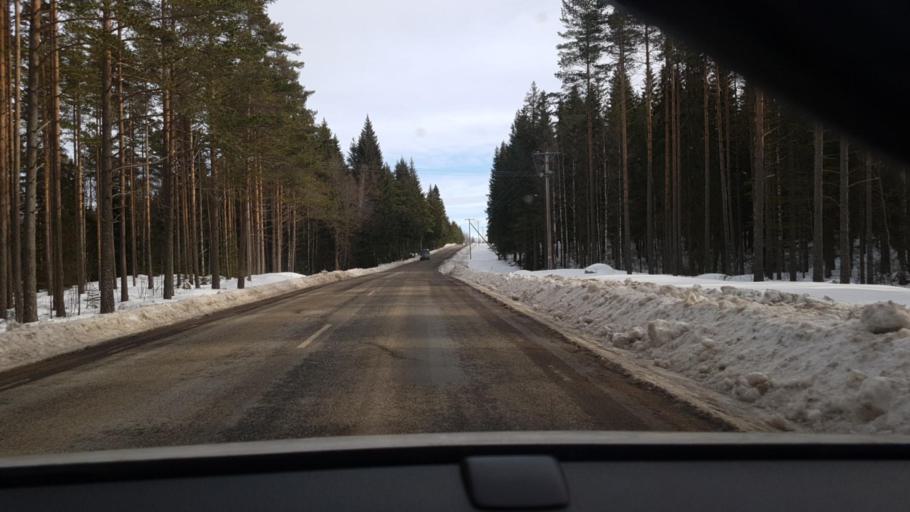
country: SE
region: Vaermland
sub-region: Arjangs Kommun
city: Arjaeng
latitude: 59.5749
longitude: 12.2150
